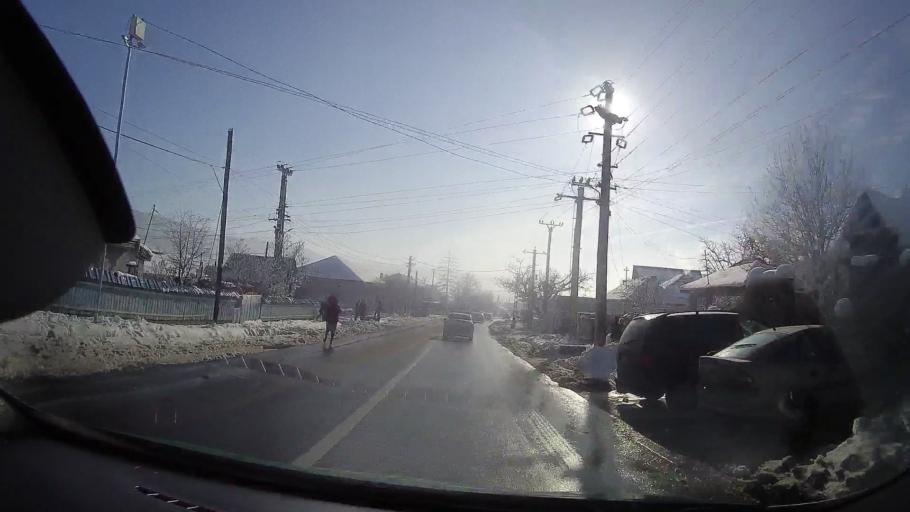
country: RO
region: Iasi
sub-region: Comuna Motca
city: Motca
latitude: 47.2464
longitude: 26.6083
